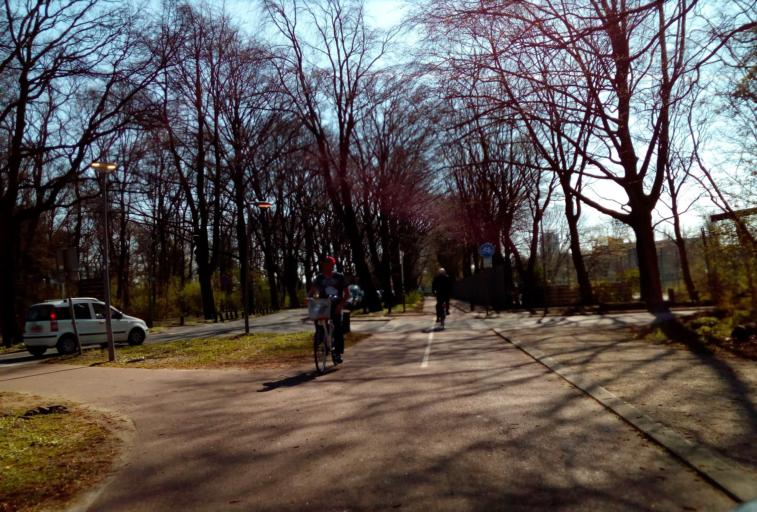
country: NL
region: South Holland
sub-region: Gemeente Rotterdam
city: Rotterdam
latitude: 51.9367
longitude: 4.5050
